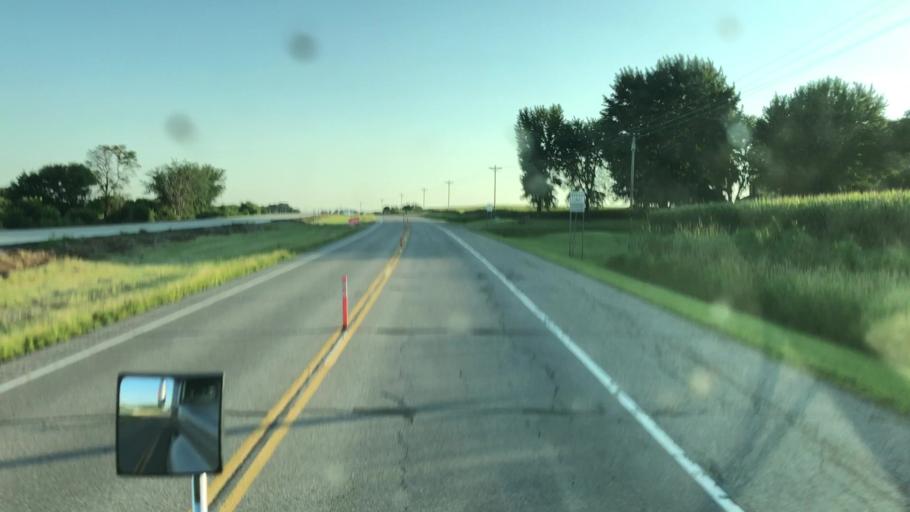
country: US
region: Minnesota
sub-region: Scott County
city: Belle Plaine
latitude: 44.5857
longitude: -93.8305
